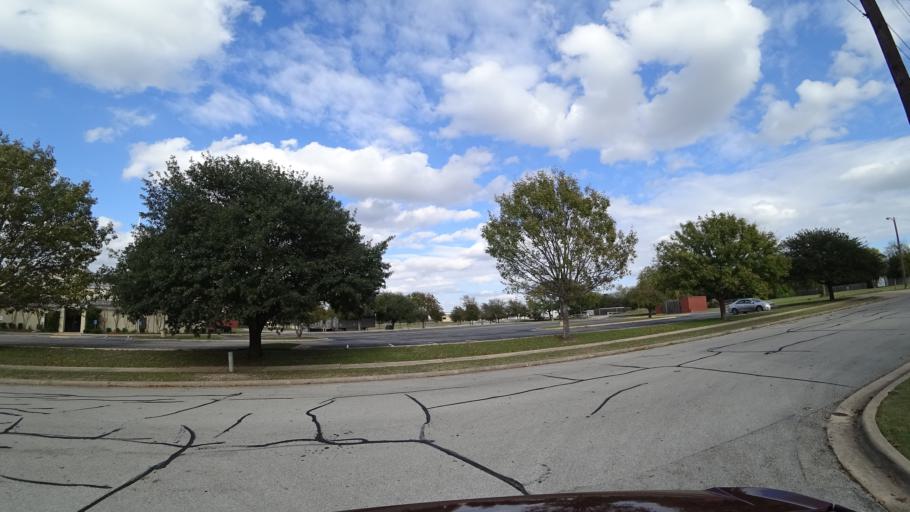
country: US
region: Texas
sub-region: Travis County
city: Pflugerville
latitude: 30.4408
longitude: -97.6272
